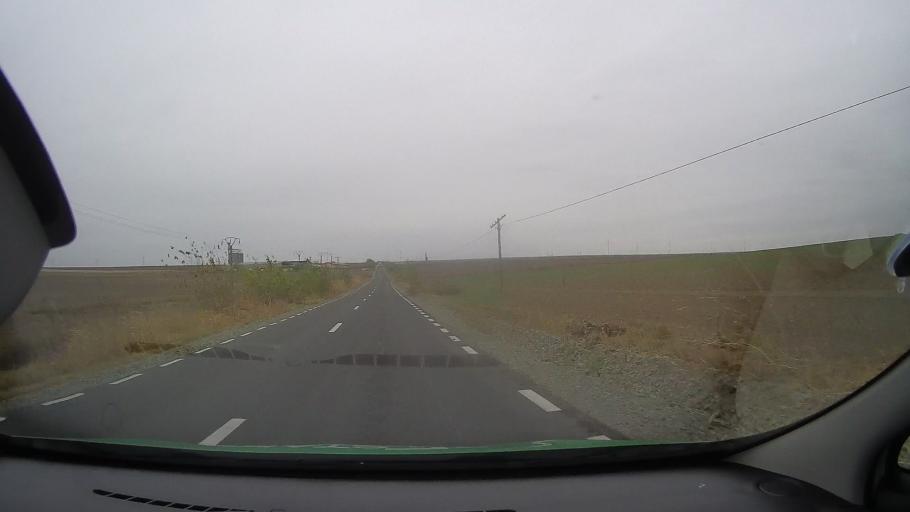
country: RO
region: Constanta
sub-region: Comuna Tortoman
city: Tortoman
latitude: 44.3604
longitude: 28.2103
